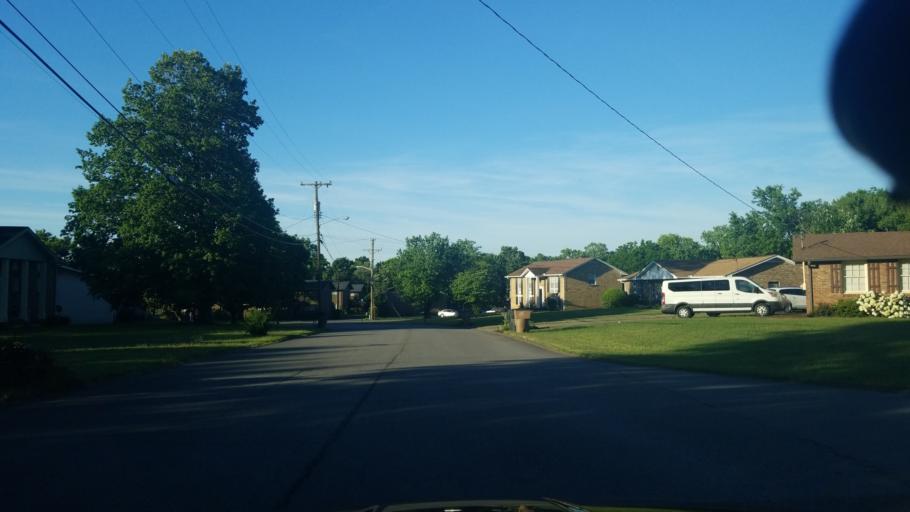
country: US
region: Tennessee
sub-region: Davidson County
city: Nashville
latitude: 36.2324
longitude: -86.7623
